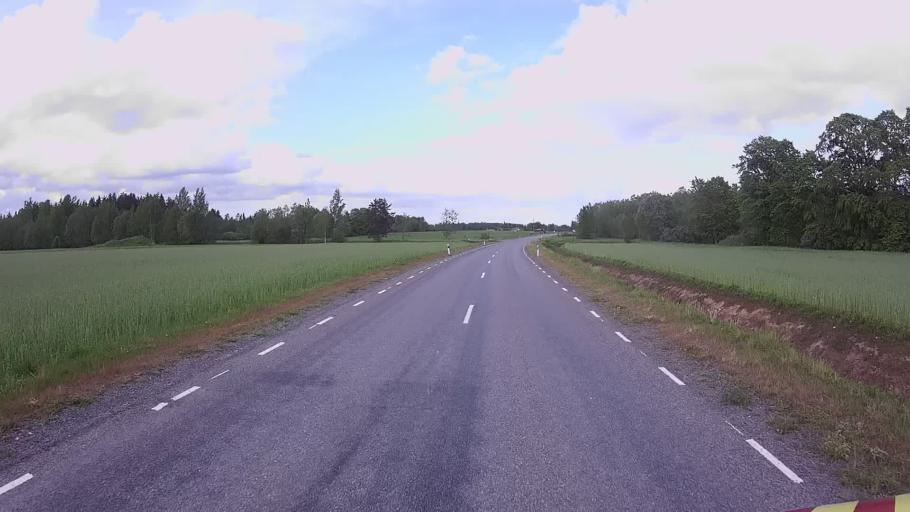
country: EE
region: Jogevamaa
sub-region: Mustvee linn
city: Mustvee
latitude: 59.0020
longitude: 26.9058
